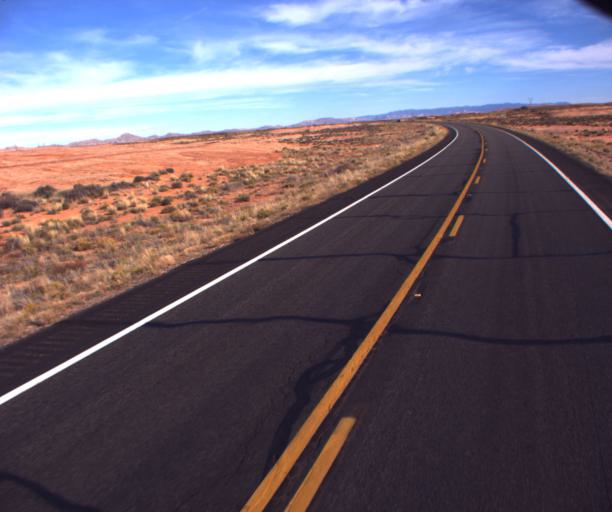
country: US
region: Arizona
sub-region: Navajo County
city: Kayenta
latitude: 36.9396
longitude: -109.7011
